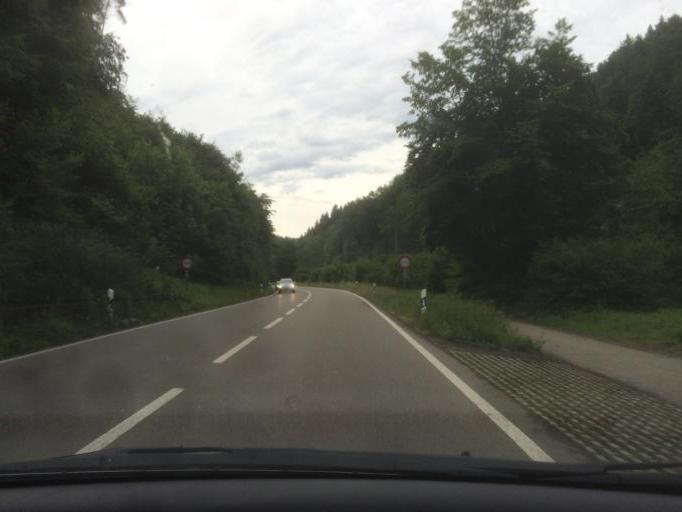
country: CH
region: Zurich
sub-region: Bezirk Uster
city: Uster / Ober-Uster
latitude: 47.3408
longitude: 8.7524
